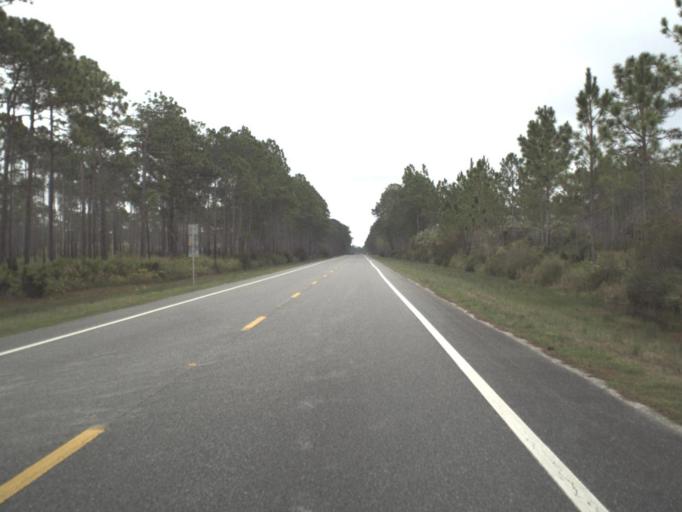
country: US
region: Florida
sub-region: Franklin County
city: Eastpoint
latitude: 29.8146
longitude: -84.8454
